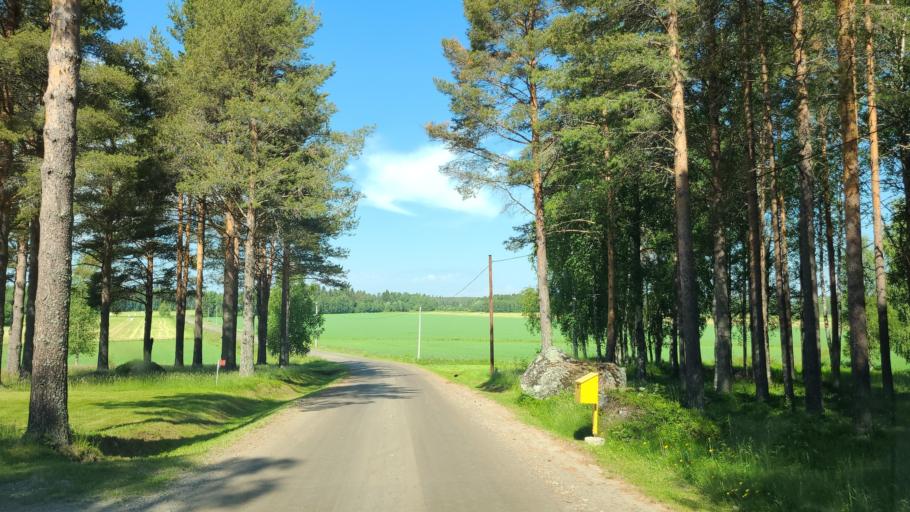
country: SE
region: Vaesterbotten
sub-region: Robertsfors Kommun
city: Robertsfors
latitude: 64.0799
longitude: 20.8565
